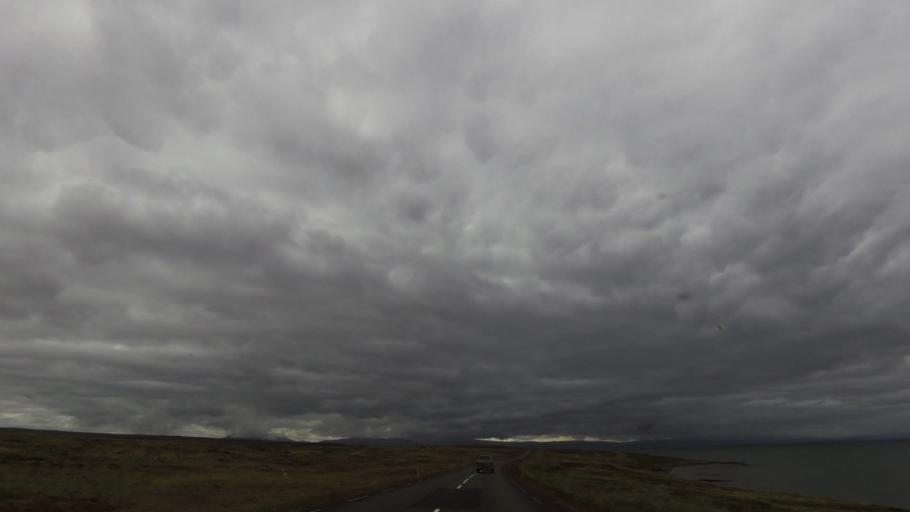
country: IS
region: West
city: Borgarnes
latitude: 65.1536
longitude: -21.7123
